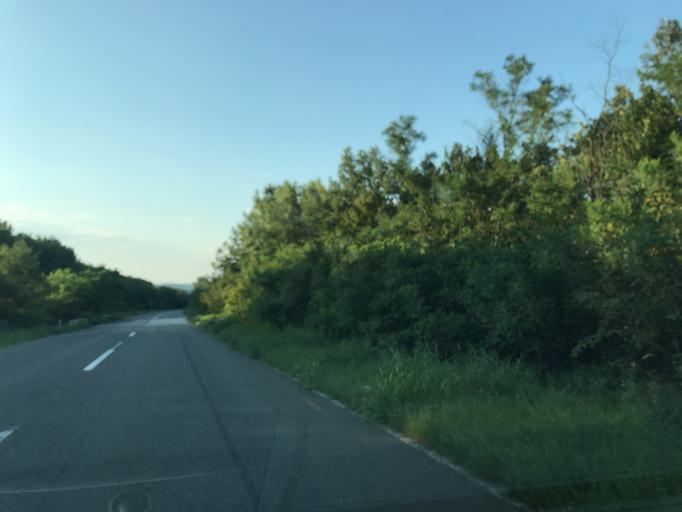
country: RO
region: Mehedinti
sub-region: Comuna Gogosu
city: Ostrovu Mare
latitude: 44.4452
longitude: 22.4548
